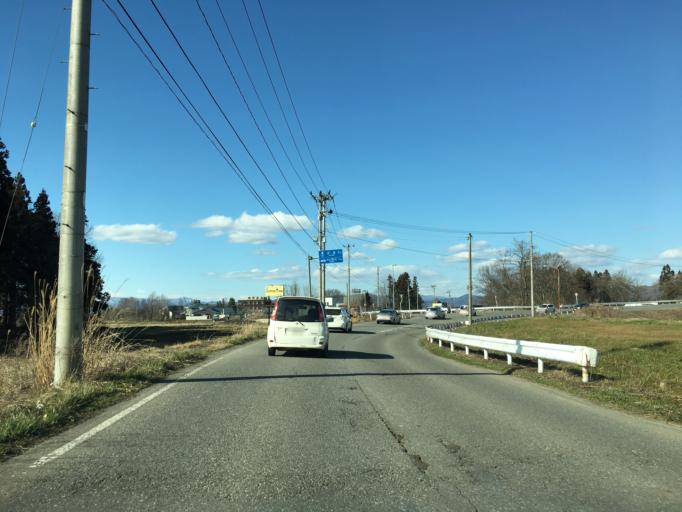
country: JP
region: Yamagata
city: Yonezawa
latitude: 37.9501
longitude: 140.1385
